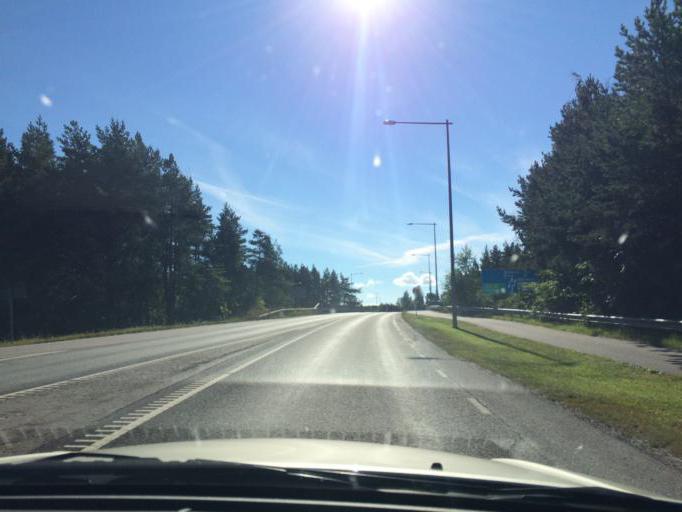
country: SE
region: Vaestmanland
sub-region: Vasteras
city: Hokasen
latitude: 59.6095
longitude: 16.6283
